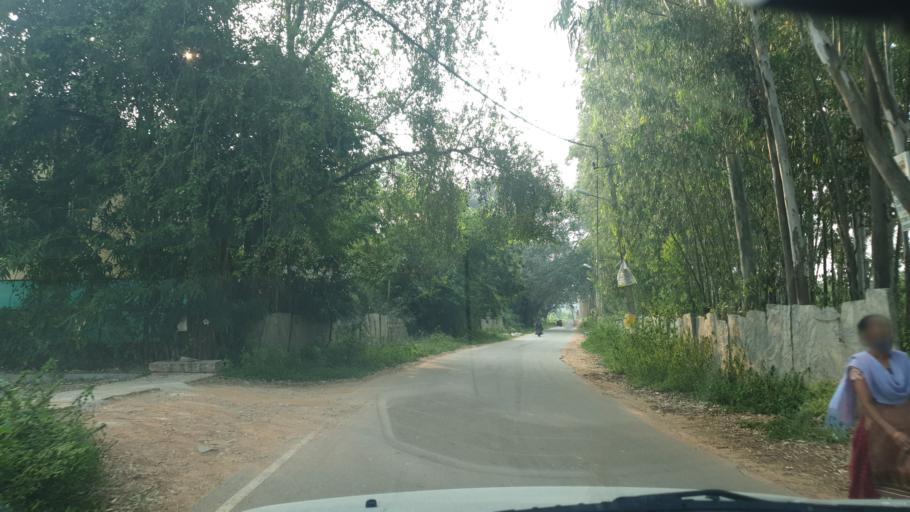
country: IN
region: Karnataka
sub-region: Bangalore Urban
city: Yelahanka
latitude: 13.0671
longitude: 77.6634
